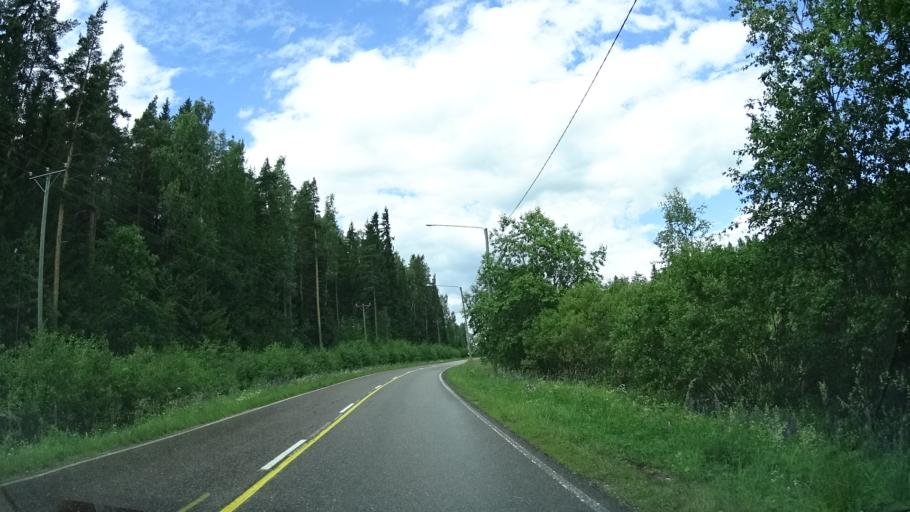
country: FI
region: Uusimaa
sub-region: Helsinki
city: Espoo
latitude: 60.3574
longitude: 24.6430
